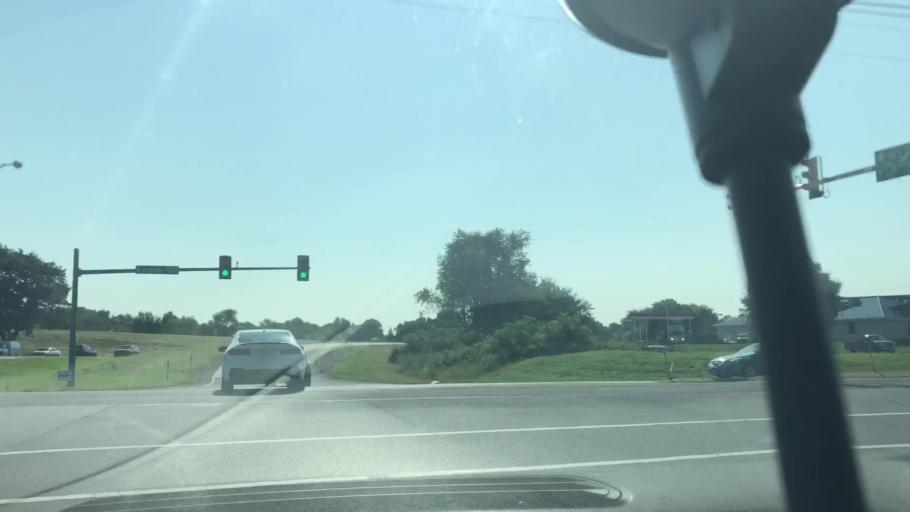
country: US
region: Pennsylvania
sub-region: Montgomery County
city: Limerick
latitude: 40.2158
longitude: -75.5458
